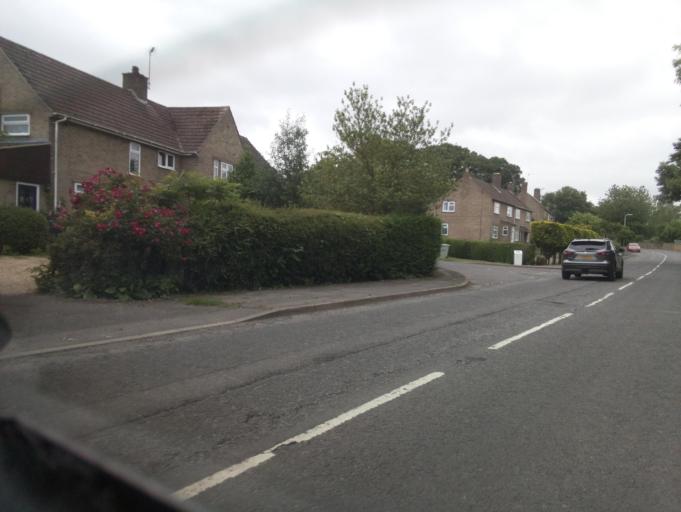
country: GB
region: England
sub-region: District of Rutland
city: Edith Weston
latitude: 52.6393
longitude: -0.6277
